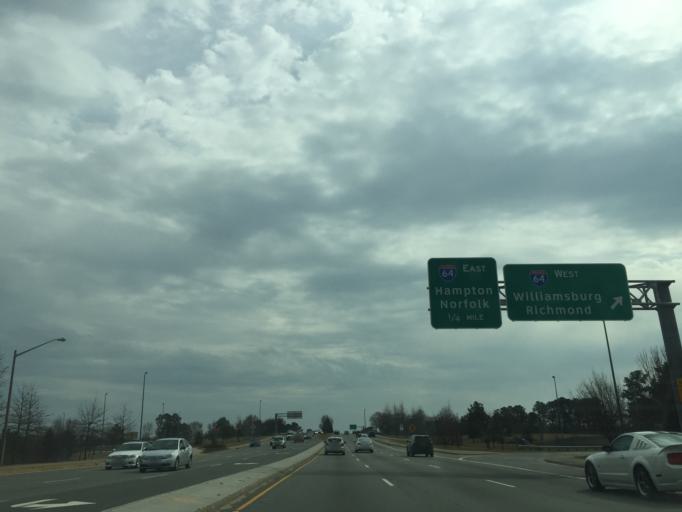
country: US
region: Virginia
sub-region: York County
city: Yorktown
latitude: 37.1193
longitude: -76.5050
